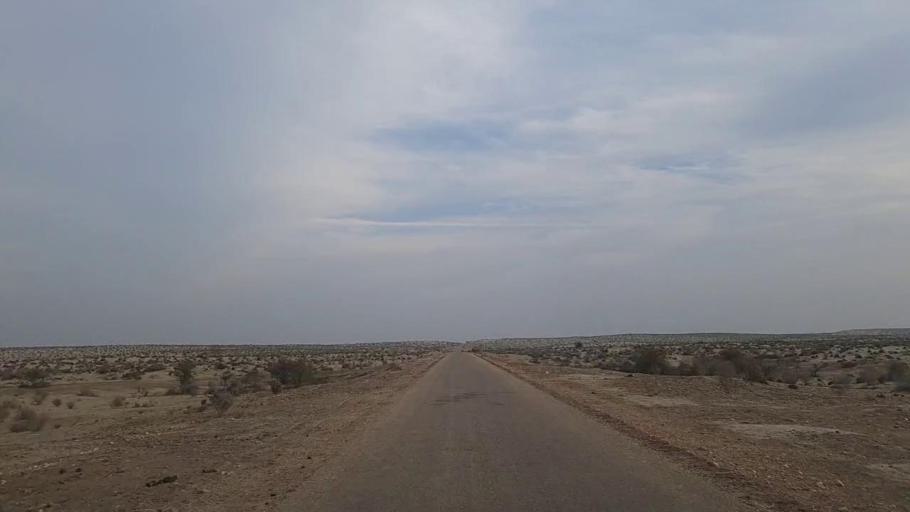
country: PK
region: Sindh
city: Daur
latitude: 26.5128
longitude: 68.5043
